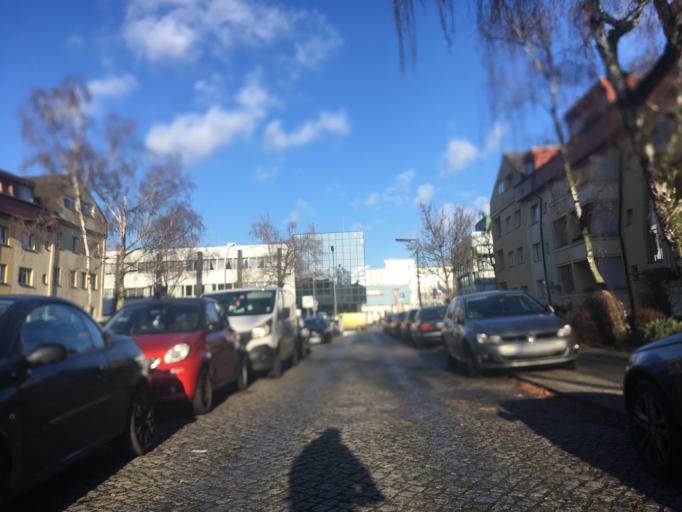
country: DE
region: Berlin
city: Reinickendorf
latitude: 52.5753
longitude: 13.3232
